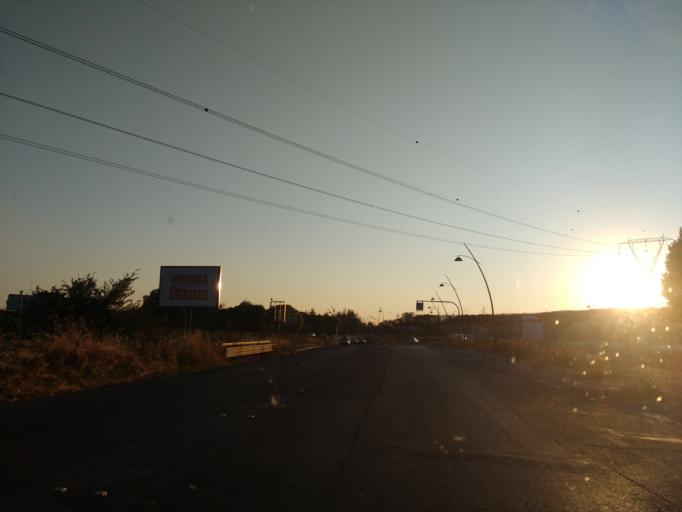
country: IT
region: Latium
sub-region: Citta metropolitana di Roma Capitale
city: Setteville
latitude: 41.9472
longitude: 12.6740
